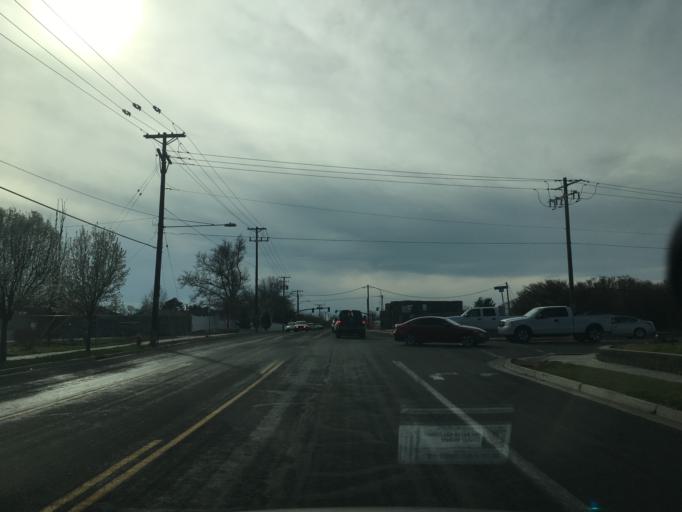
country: US
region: Utah
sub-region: Davis County
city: Layton
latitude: 41.0602
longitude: -111.9857
